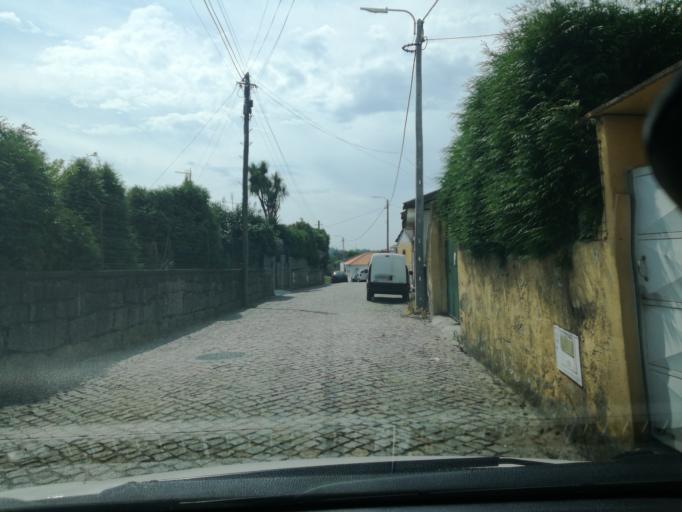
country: PT
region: Porto
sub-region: Vila Nova de Gaia
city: Grijo
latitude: 41.0265
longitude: -8.5893
